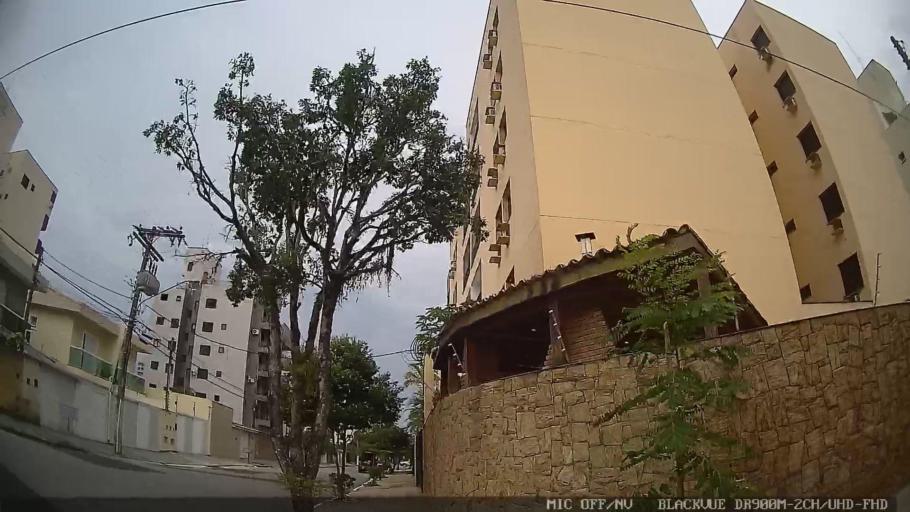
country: BR
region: Sao Paulo
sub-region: Guaruja
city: Guaruja
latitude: -23.9782
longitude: -46.2230
